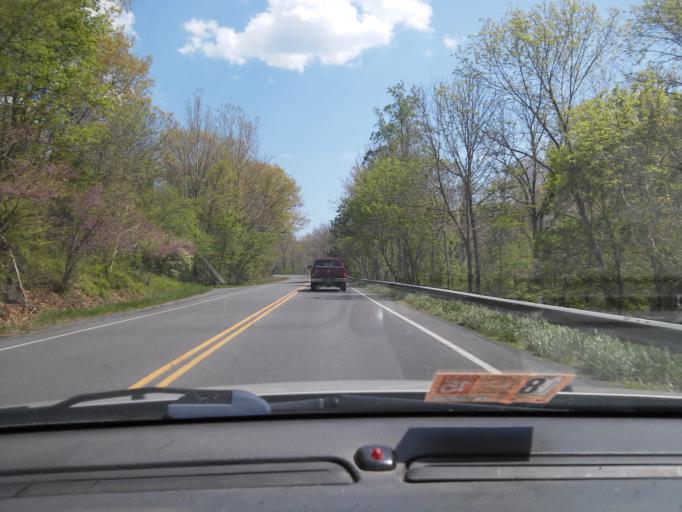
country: US
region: Virginia
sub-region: Warren County
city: Front Royal
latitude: 38.8919
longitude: -78.1739
